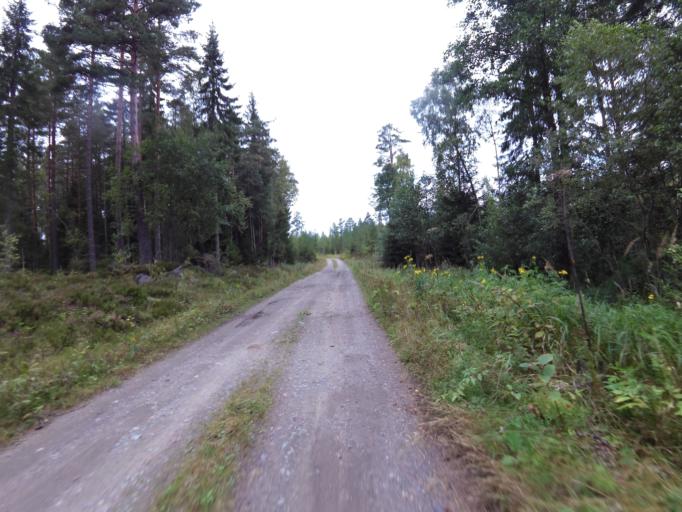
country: SE
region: Gaevleborg
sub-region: Gavle Kommun
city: Valbo
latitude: 60.7474
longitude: 16.9823
